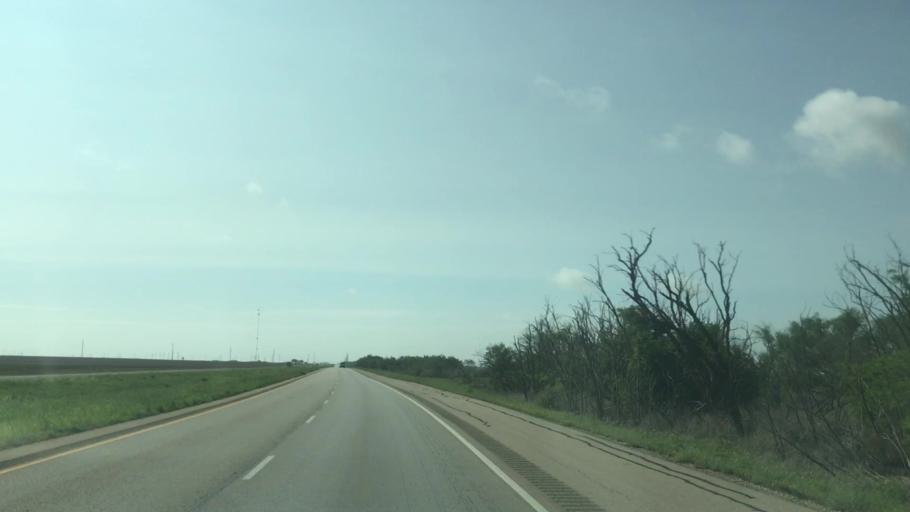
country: US
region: Texas
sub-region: Nolan County
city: Roscoe
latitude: 32.5742
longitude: -100.7201
